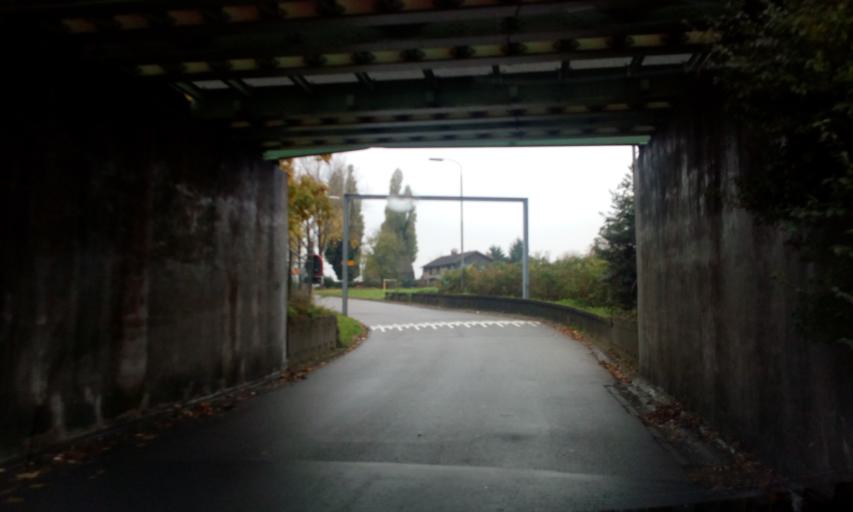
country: NL
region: South Holland
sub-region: Gemeente Lansingerland
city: Berkel en Rodenrijs
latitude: 51.9773
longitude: 4.4605
